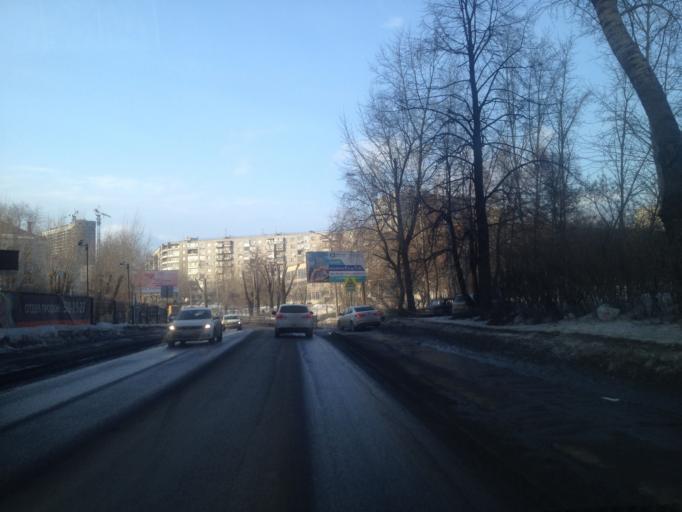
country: RU
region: Sverdlovsk
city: Yekaterinburg
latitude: 56.8506
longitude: 60.5869
